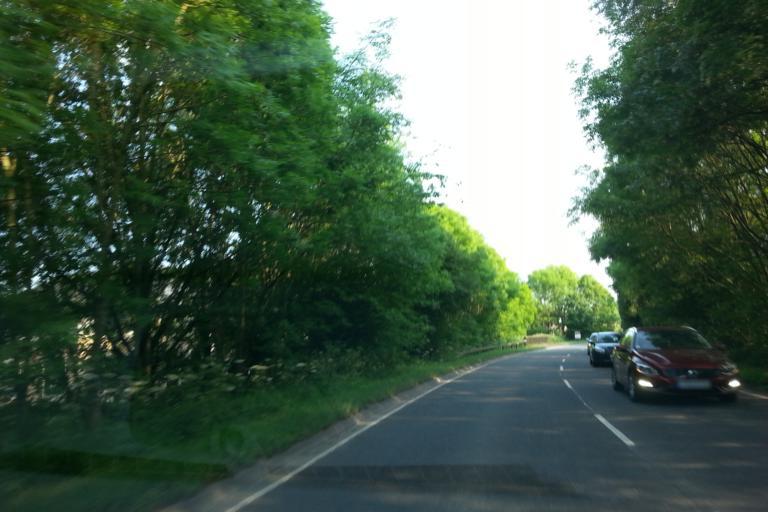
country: GB
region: England
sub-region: Cambridgeshire
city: Needingworth
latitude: 52.3297
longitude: -0.0592
